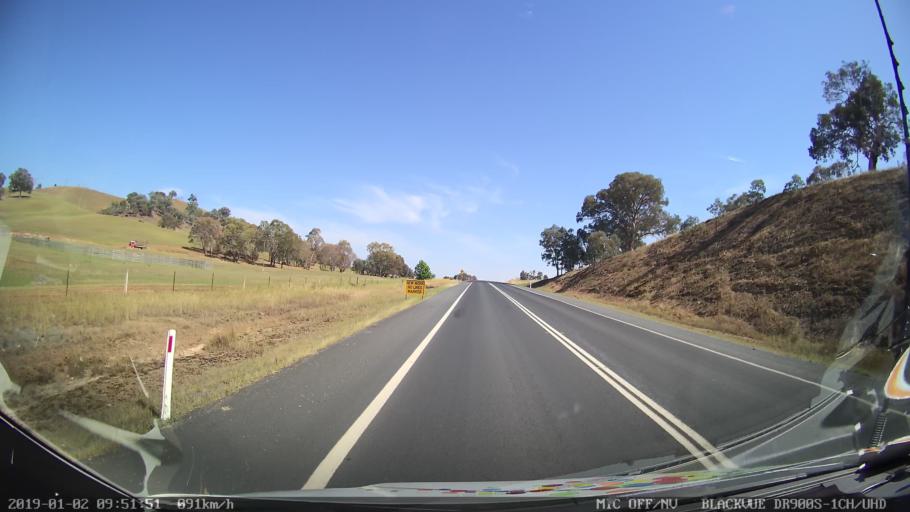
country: AU
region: New South Wales
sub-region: Tumut Shire
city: Tumut
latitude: -35.2676
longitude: 148.2109
